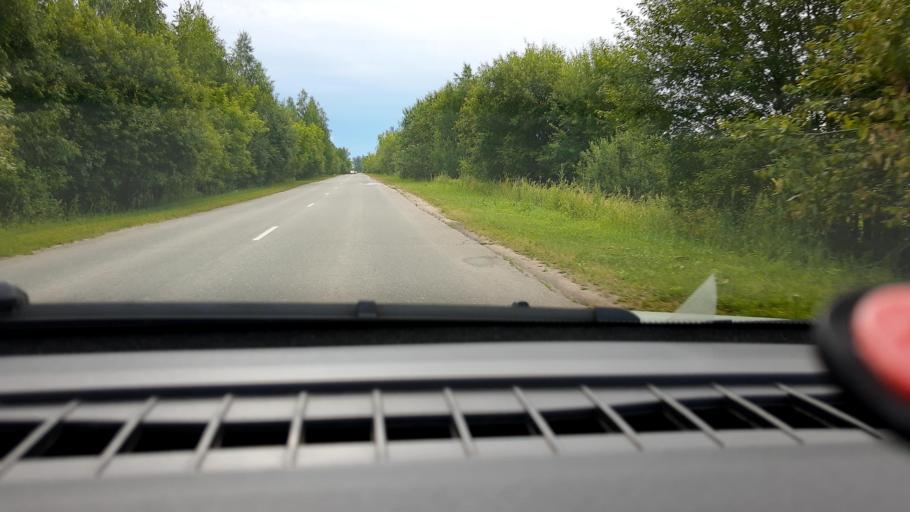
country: RU
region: Nizjnij Novgorod
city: Kstovo
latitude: 56.1500
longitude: 44.2981
